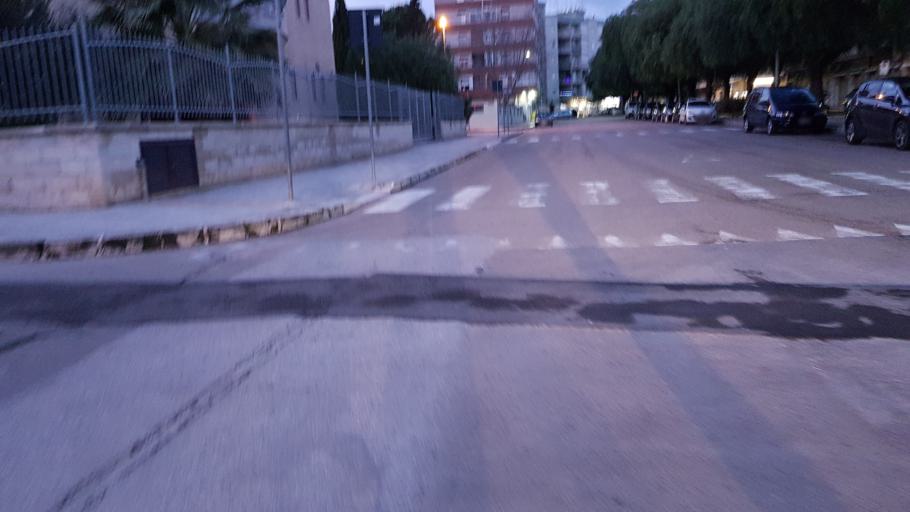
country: IT
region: Apulia
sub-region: Provincia di Brindisi
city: Brindisi
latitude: 40.6238
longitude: 17.9253
